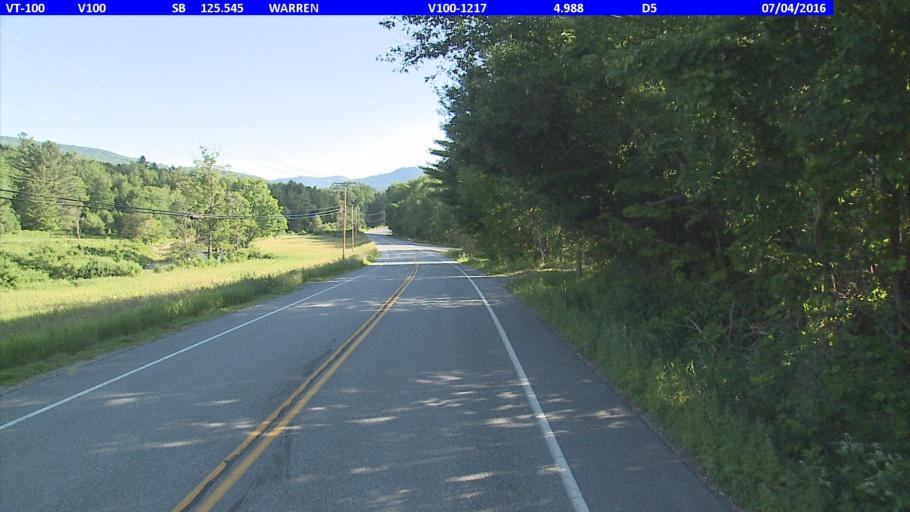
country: US
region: Vermont
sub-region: Washington County
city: Northfield
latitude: 44.1288
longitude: -72.8505
